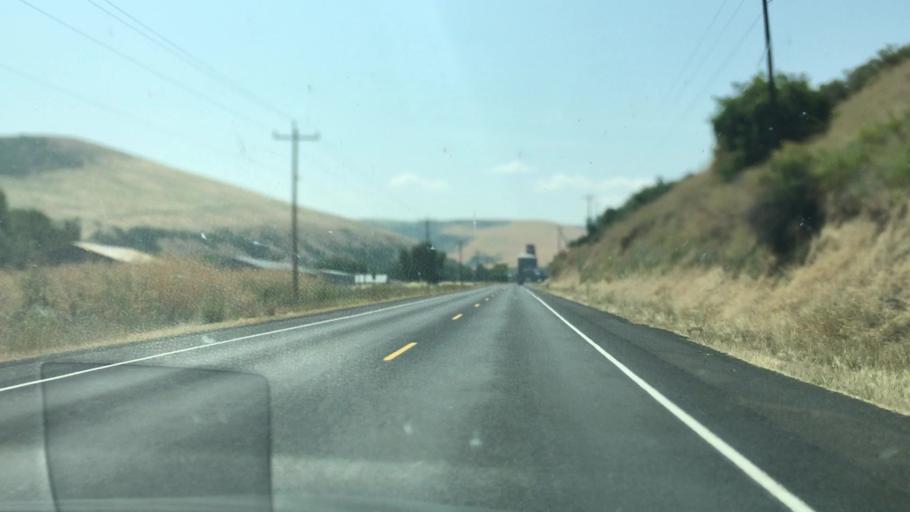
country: US
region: Idaho
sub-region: Nez Perce County
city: Lapwai
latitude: 46.3805
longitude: -116.7961
